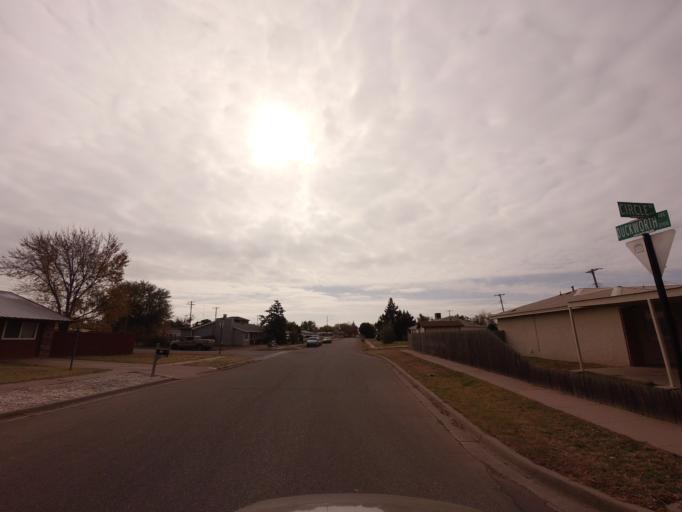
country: US
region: New Mexico
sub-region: Curry County
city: Clovis
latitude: 34.4298
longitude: -103.2168
